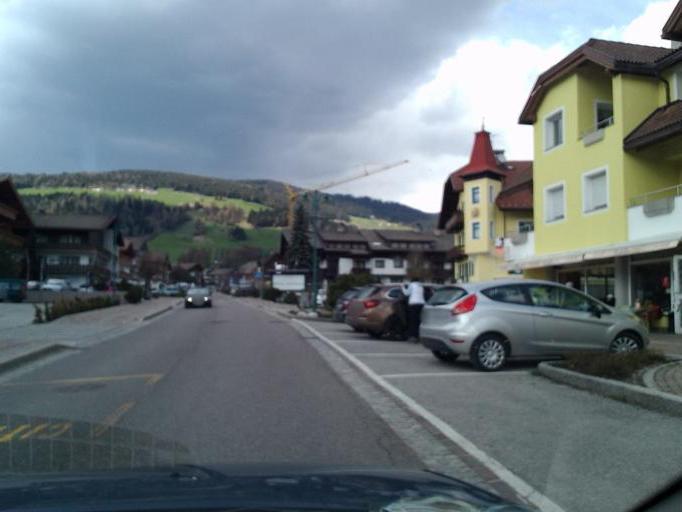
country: IT
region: Trentino-Alto Adige
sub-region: Bolzano
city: Dobbiaco
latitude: 46.7305
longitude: 12.2237
